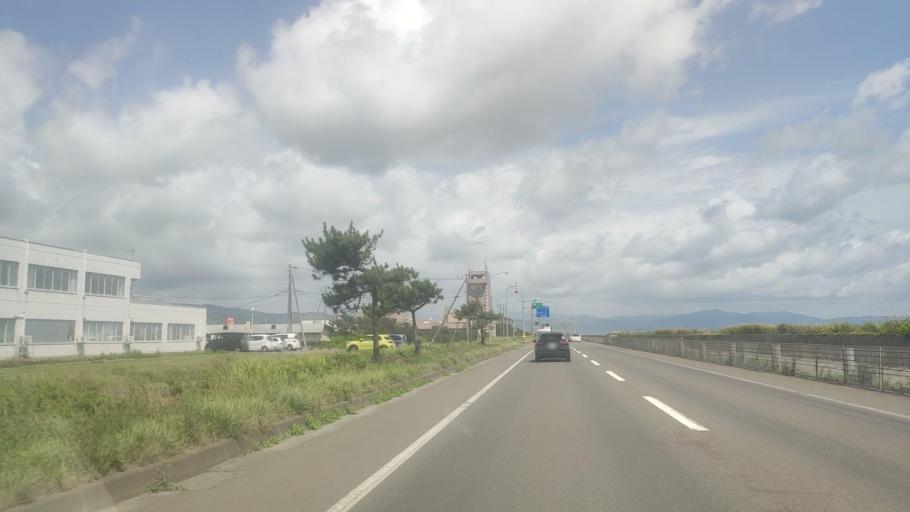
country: JP
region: Hokkaido
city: Niseko Town
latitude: 42.5098
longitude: 140.3773
